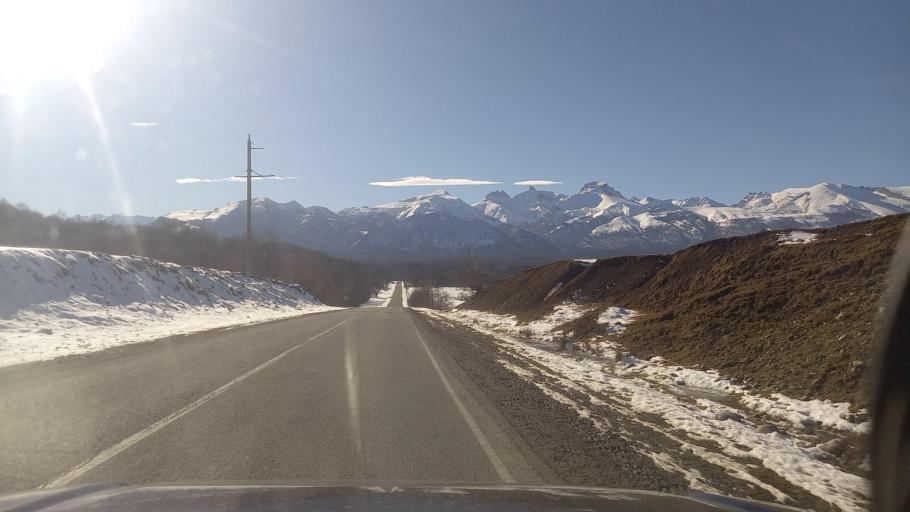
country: RU
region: North Ossetia
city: Chikola
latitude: 43.1335
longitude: 43.8238
